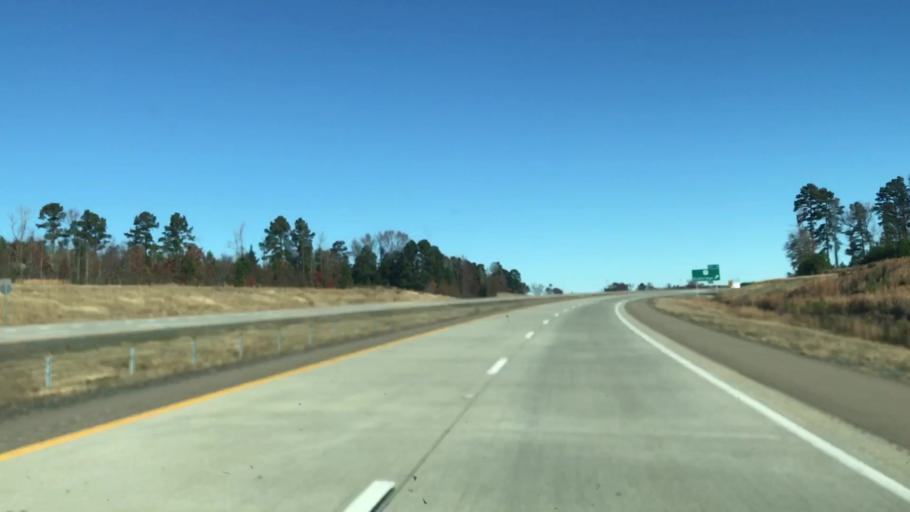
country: US
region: Louisiana
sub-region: Caddo Parish
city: Vivian
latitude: 33.0735
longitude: -93.9048
